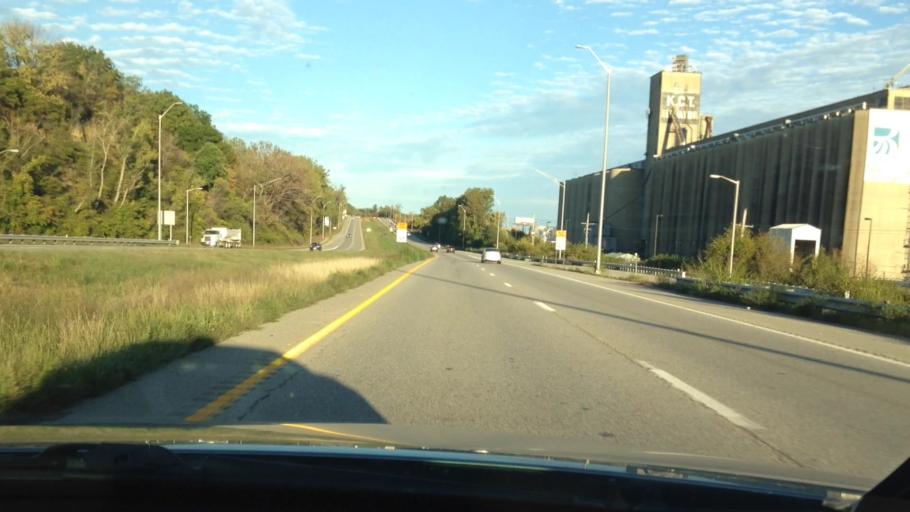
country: US
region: Missouri
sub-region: Clay County
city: North Kansas City
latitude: 39.1541
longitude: -94.5154
